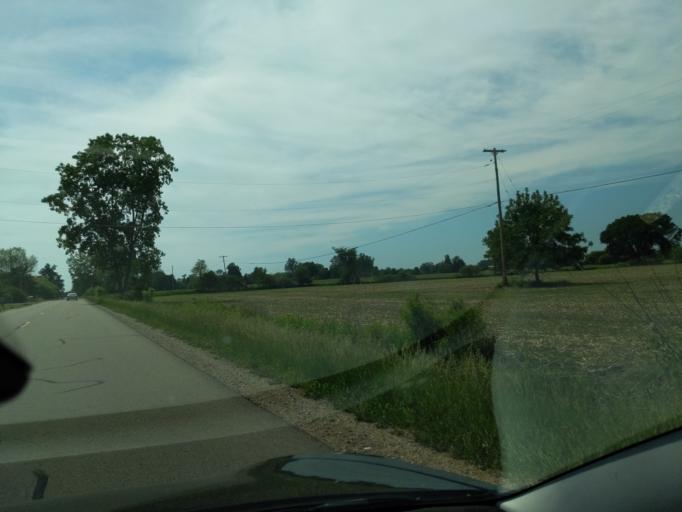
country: US
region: Michigan
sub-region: Eaton County
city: Grand Ledge
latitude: 42.7119
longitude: -84.7735
